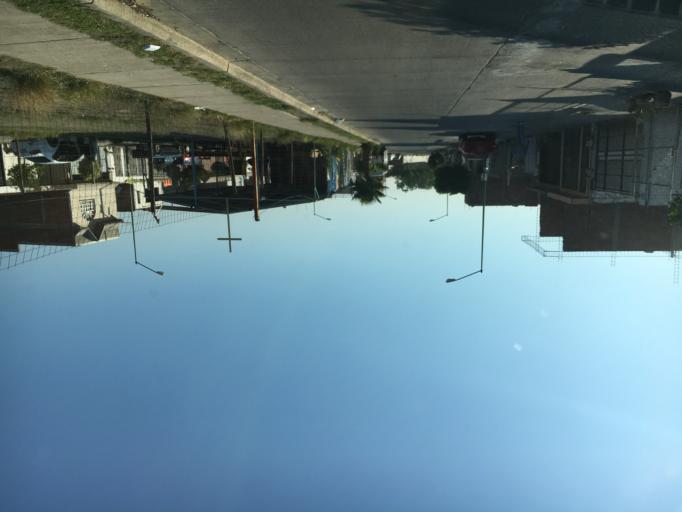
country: MX
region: Guanajuato
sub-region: Leon
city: Fraccionamiento Paraiso Real
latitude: 21.1031
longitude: -101.6074
